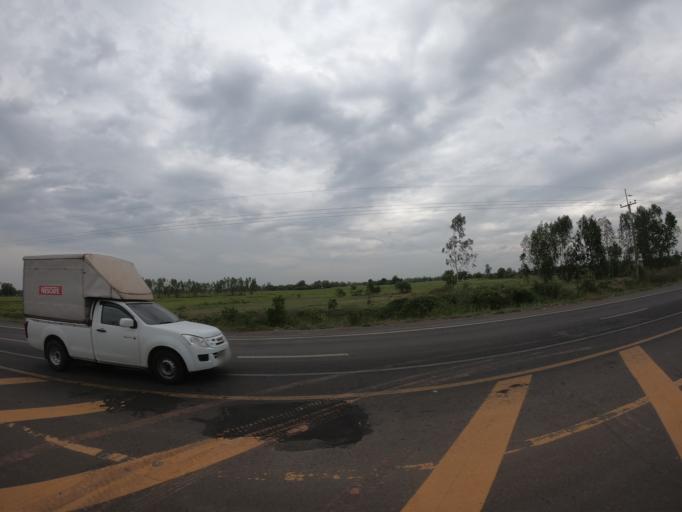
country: TH
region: Roi Et
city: Thawat Buri
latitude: 16.0947
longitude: 103.7872
